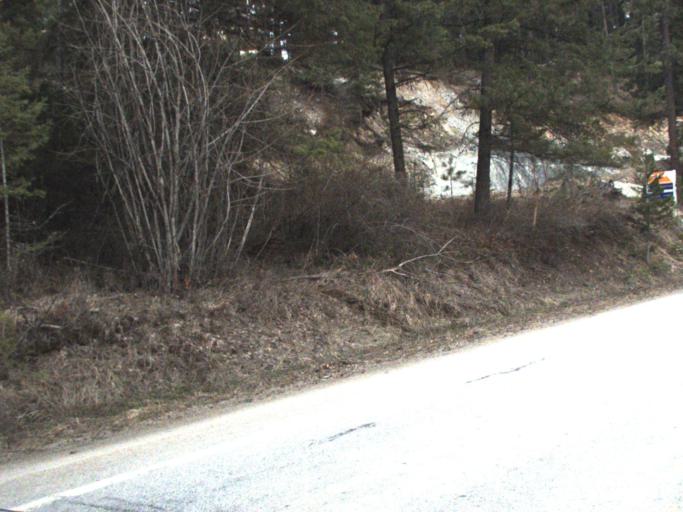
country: US
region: Washington
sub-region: Pend Oreille County
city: Newport
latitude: 48.1873
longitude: -117.0490
